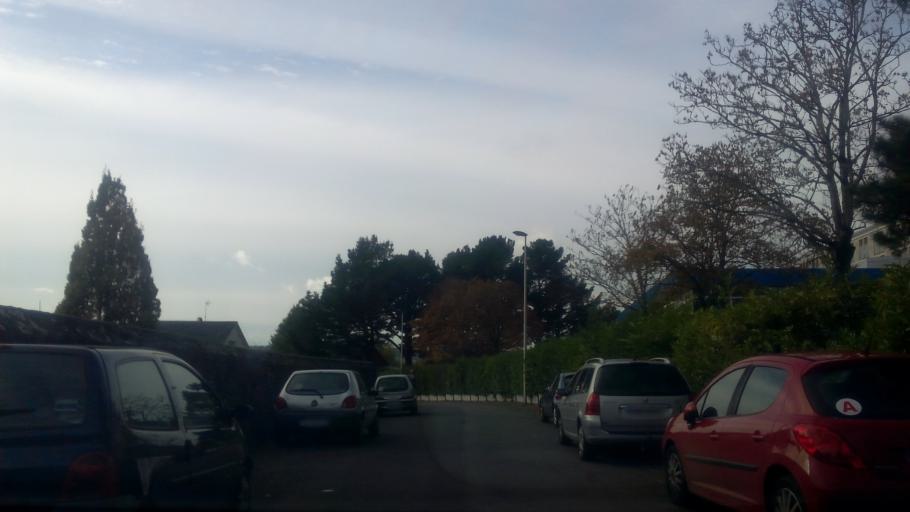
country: FR
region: Brittany
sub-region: Departement d'Ille-et-Vilaine
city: Redon
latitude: 47.6547
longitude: -2.0901
